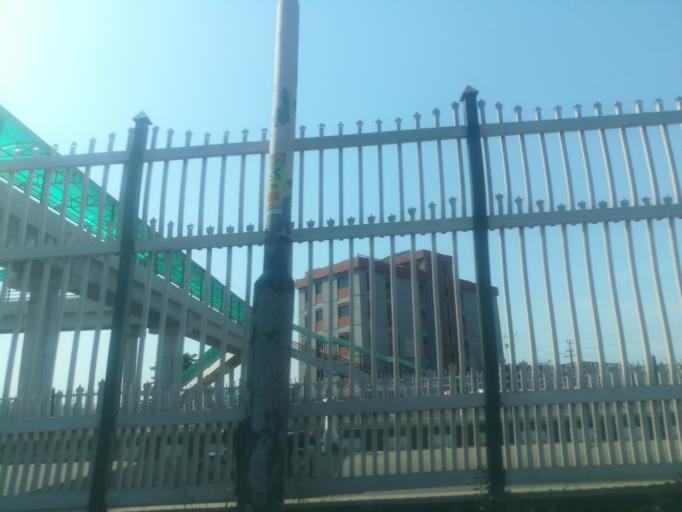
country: NG
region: Ogun
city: Abeokuta
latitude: 7.1357
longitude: 3.3320
